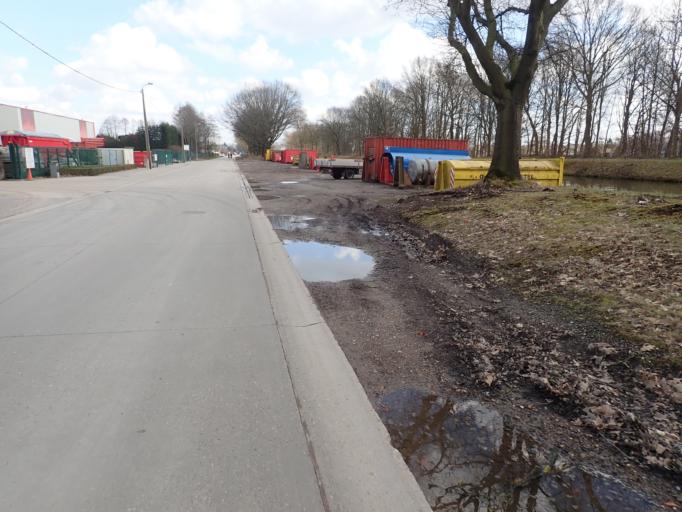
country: BE
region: Flanders
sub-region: Provincie Antwerpen
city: Beerse
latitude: 51.3268
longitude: 4.8465
